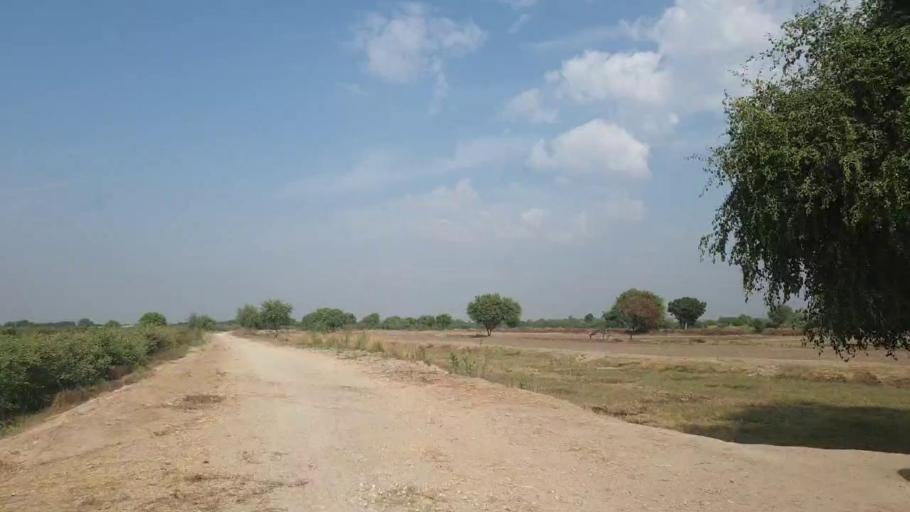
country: PK
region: Sindh
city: Digri
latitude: 25.0144
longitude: 69.0668
